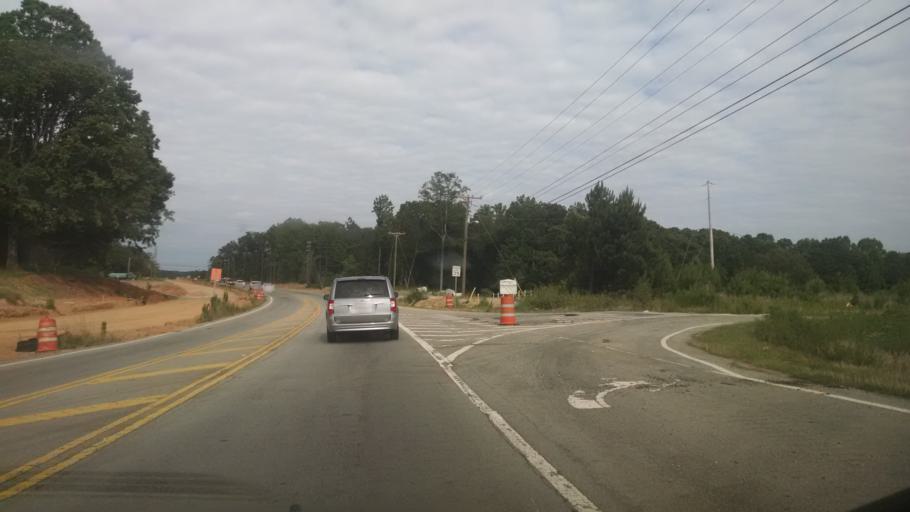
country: US
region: Georgia
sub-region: Gwinnett County
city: Sugar Hill
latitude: 34.1124
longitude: -84.0713
